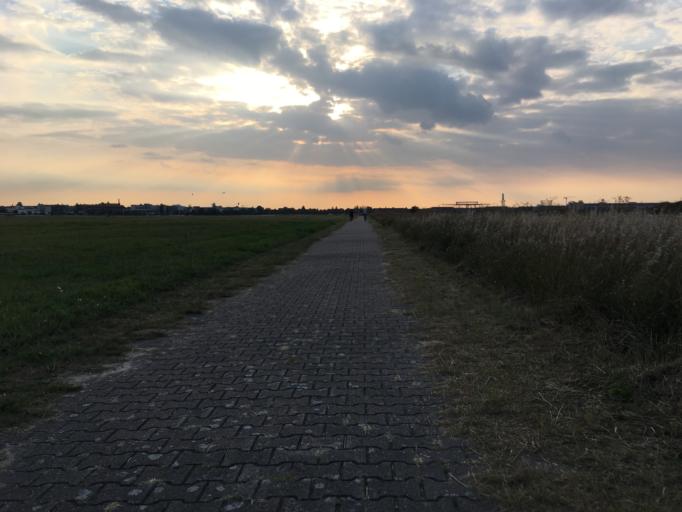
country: DE
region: Berlin
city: Tempelhof Bezirk
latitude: 52.4727
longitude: 13.4110
